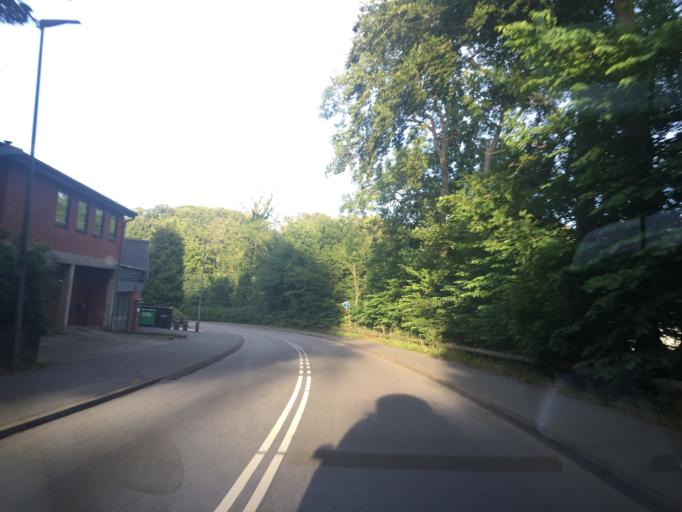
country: DK
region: South Denmark
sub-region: Kolding Kommune
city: Kolding
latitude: 55.4767
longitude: 9.5088
